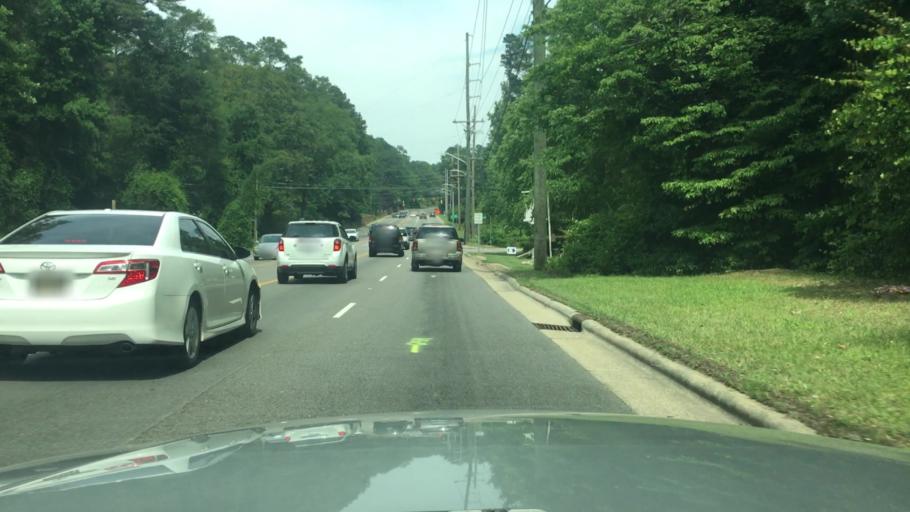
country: US
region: North Carolina
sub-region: Cumberland County
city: Fayetteville
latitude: 35.0637
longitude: -78.9303
